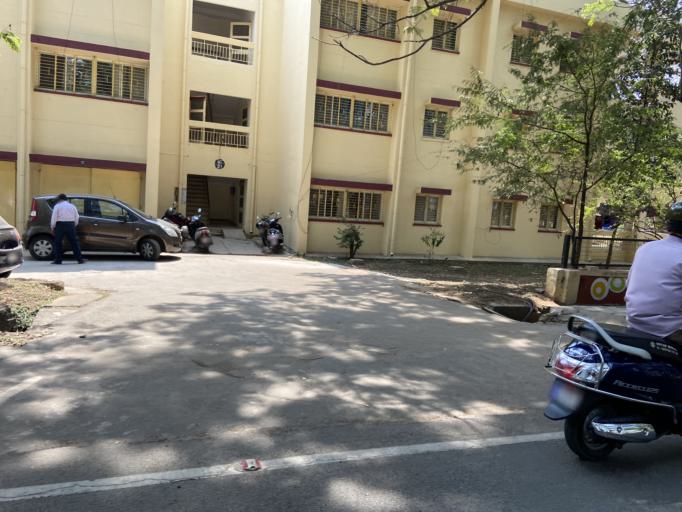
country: IN
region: Karnataka
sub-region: Bangalore Urban
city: Bangalore
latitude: 12.9835
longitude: 77.6593
